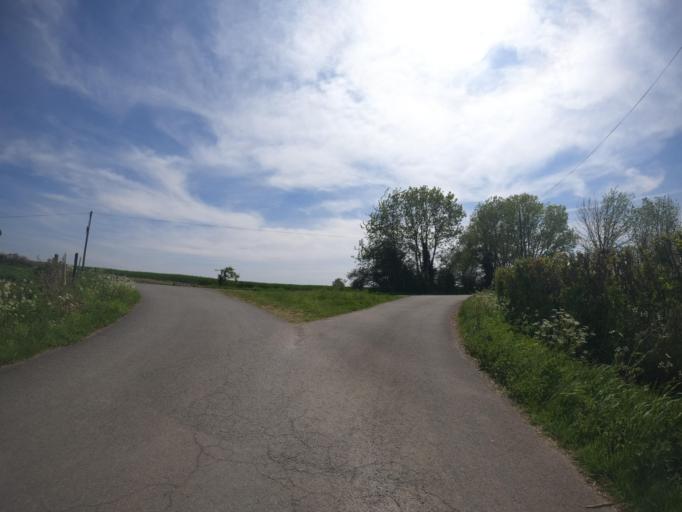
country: FR
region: Poitou-Charentes
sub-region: Departement des Deux-Sevres
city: Secondigny
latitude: 46.6483
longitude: -0.4980
